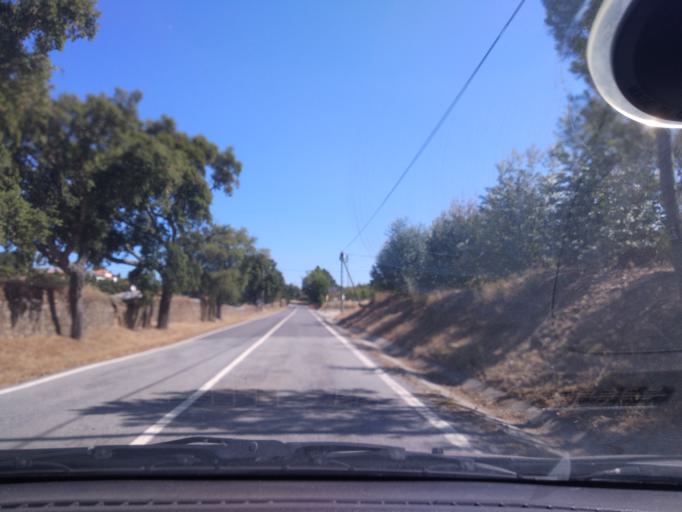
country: PT
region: Castelo Branco
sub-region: Castelo Branco
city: Castelo Branco
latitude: 39.7439
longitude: -7.6209
